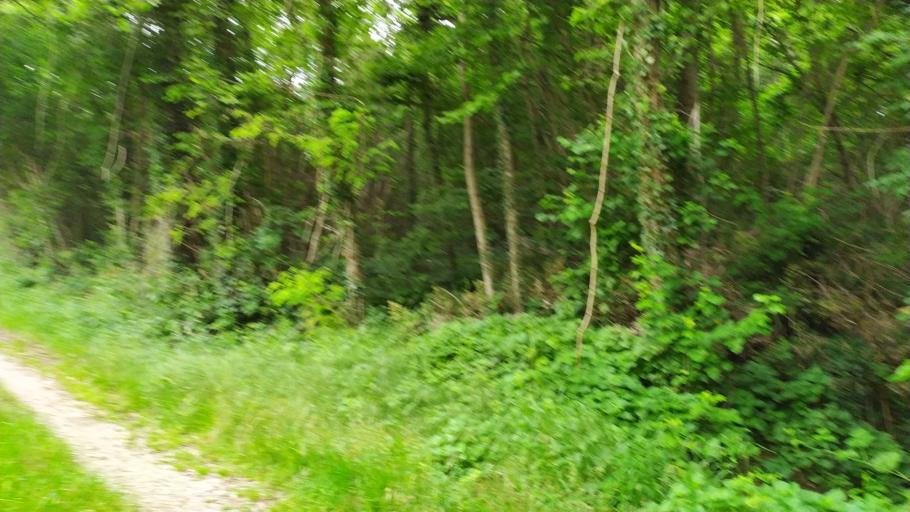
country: IT
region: Friuli Venezia Giulia
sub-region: Provincia di Udine
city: Majano
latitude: 46.1905
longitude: 13.0401
